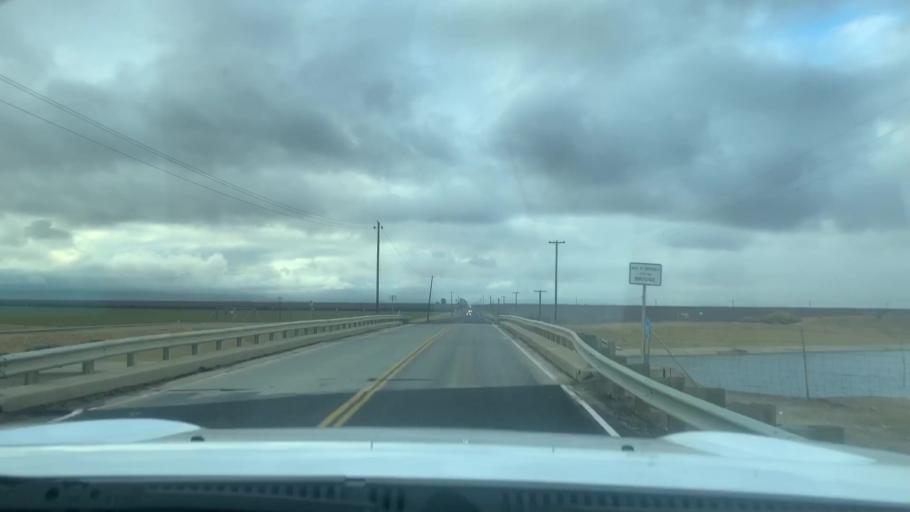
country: US
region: California
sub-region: Kern County
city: Lost Hills
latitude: 35.4993
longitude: -119.6472
